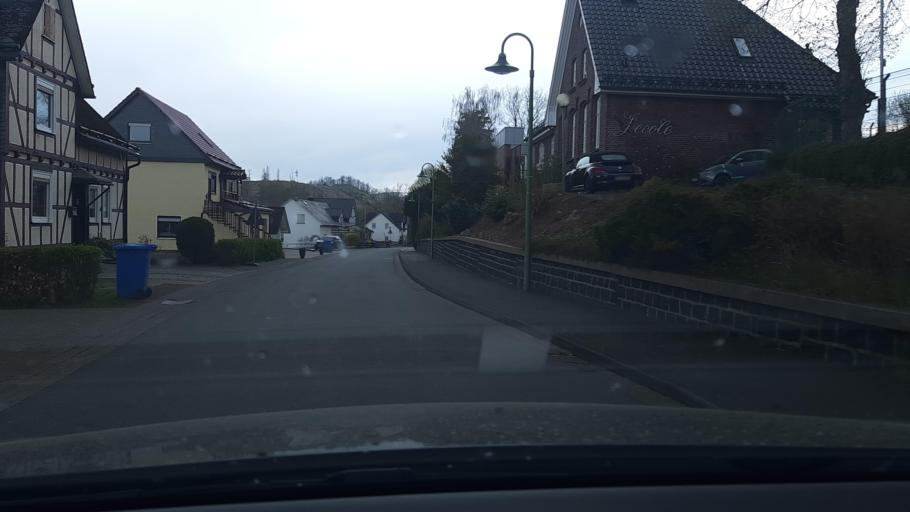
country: DE
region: North Rhine-Westphalia
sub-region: Regierungsbezirk Arnsberg
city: Bad Laasphe
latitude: 50.8857
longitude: 8.3655
